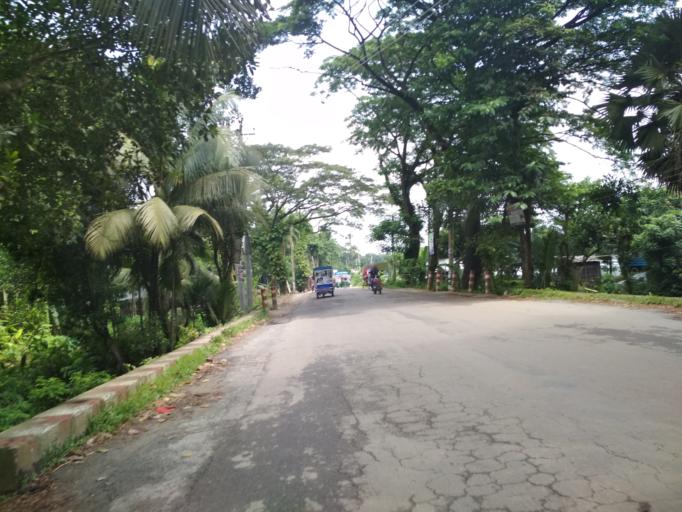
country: BD
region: Chittagong
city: Lakshmipur
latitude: 22.9650
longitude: 90.8097
